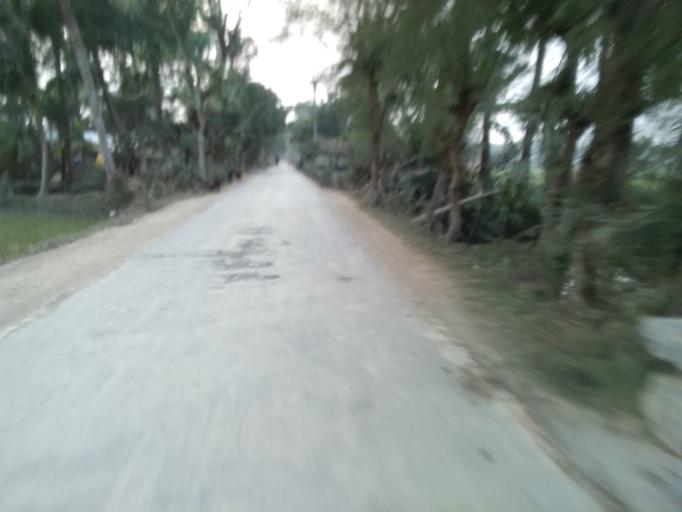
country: BD
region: Khulna
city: Satkhira
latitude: 22.6505
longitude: 89.0013
